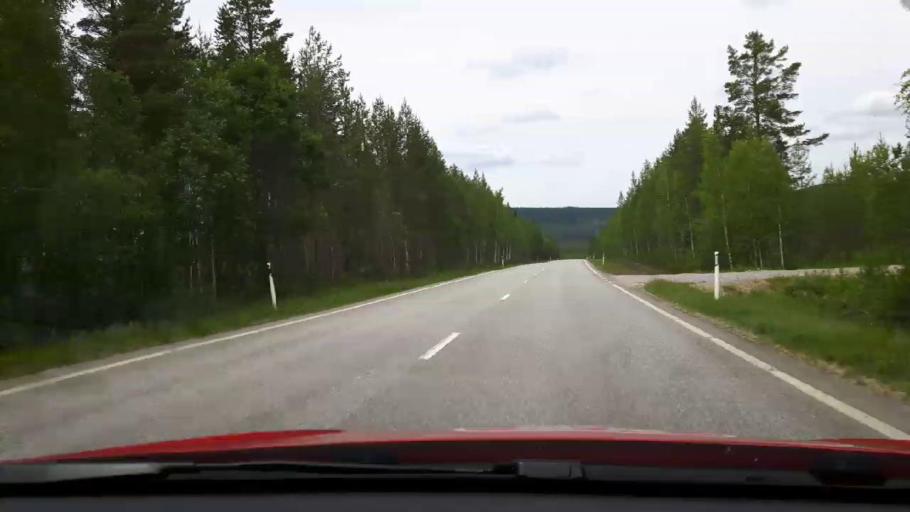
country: SE
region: Jaemtland
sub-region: Harjedalens Kommun
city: Sveg
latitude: 62.0838
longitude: 14.2537
